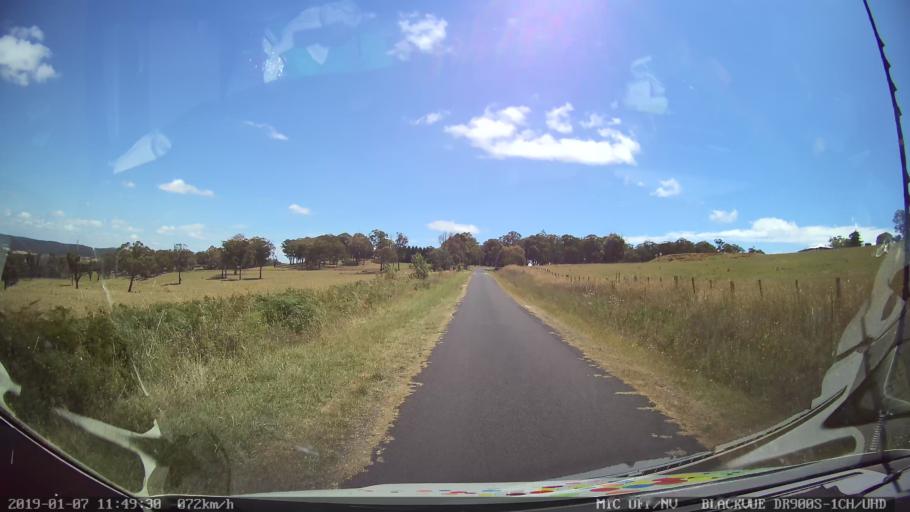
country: AU
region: New South Wales
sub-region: Guyra
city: Guyra
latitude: -30.3183
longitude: 151.6289
